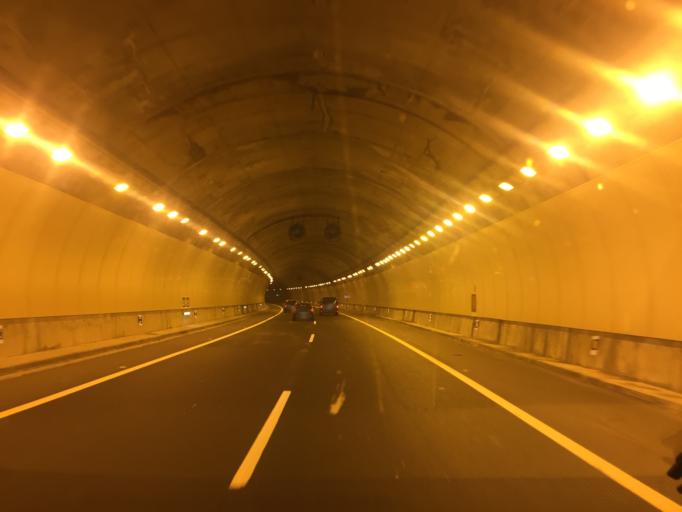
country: ES
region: Andalusia
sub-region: Provincia de Malaga
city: Nerja
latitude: 36.7663
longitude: -3.8633
